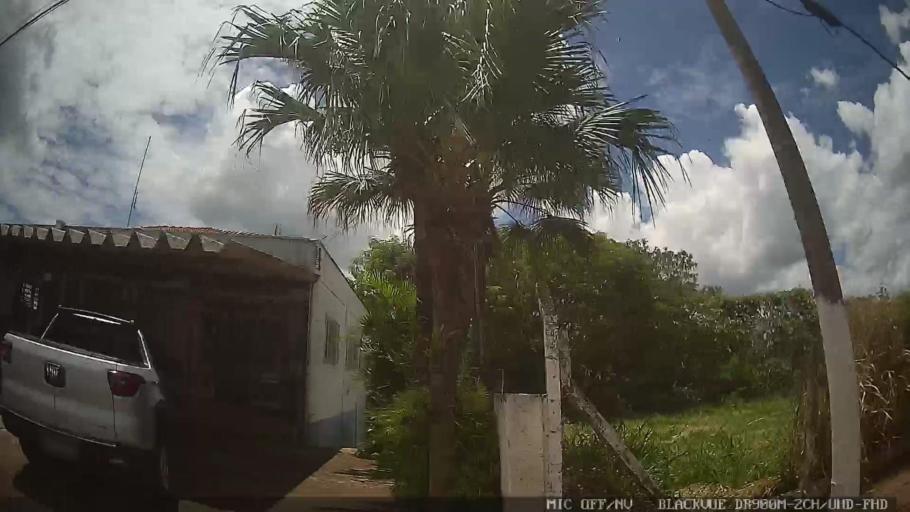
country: BR
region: Sao Paulo
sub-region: Laranjal Paulista
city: Laranjal Paulista
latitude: -23.0396
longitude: -47.8920
